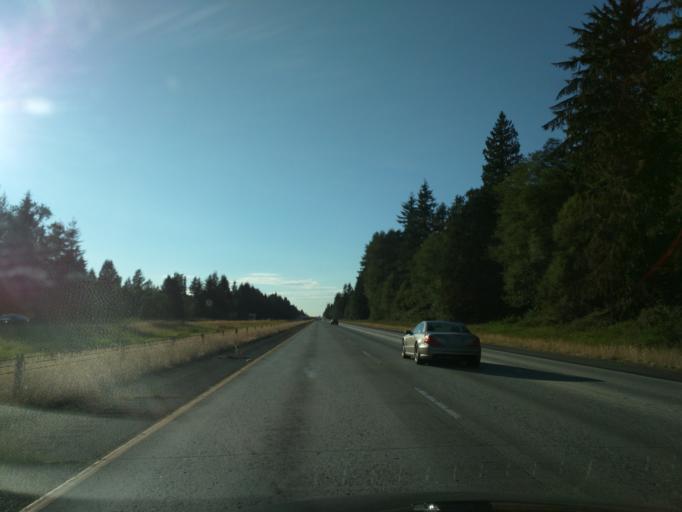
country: US
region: Washington
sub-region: Snohomish County
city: Stanwood
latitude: 48.2804
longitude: -122.2834
